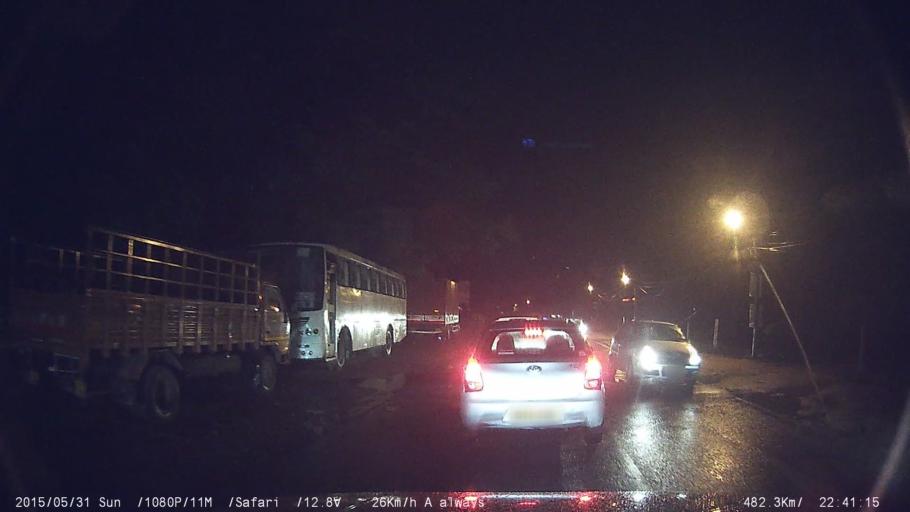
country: IN
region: Karnataka
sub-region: Bangalore Urban
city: Bangalore
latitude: 12.8587
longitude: 77.5891
